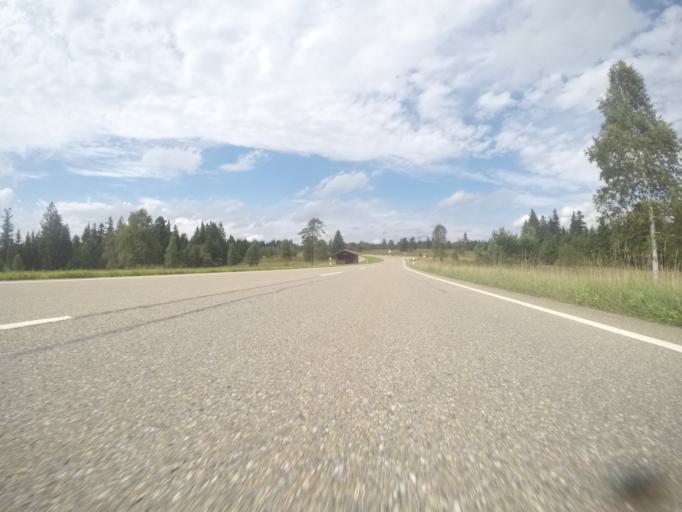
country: DE
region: Baden-Wuerttemberg
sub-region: Freiburg Region
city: Bad Peterstal-Griesbach
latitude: 48.4902
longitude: 8.2693
